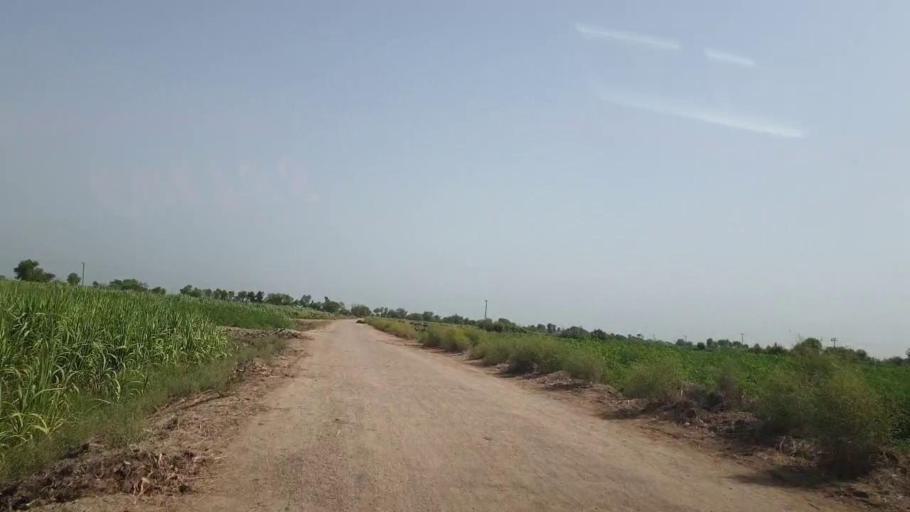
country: PK
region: Sindh
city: Daur
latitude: 26.3172
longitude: 68.2154
